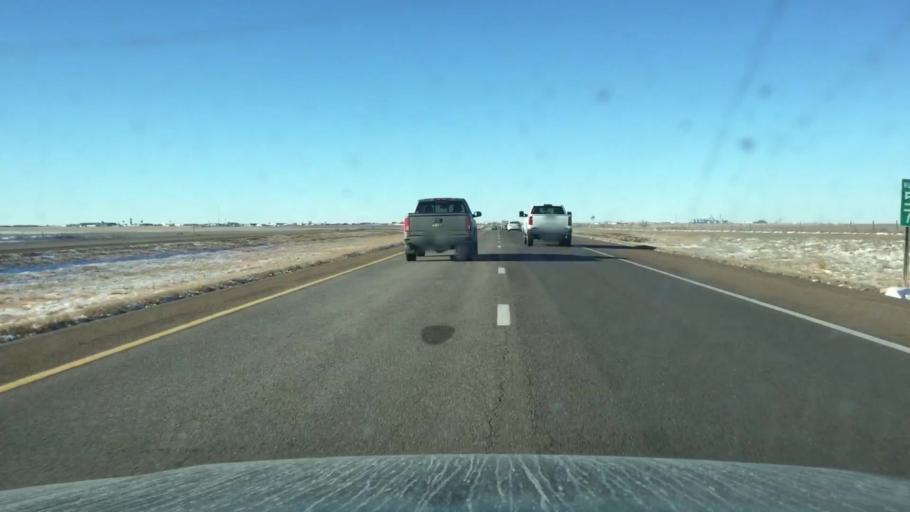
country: US
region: Kansas
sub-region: Thomas County
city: Colby
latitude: 39.3419
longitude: -101.0119
